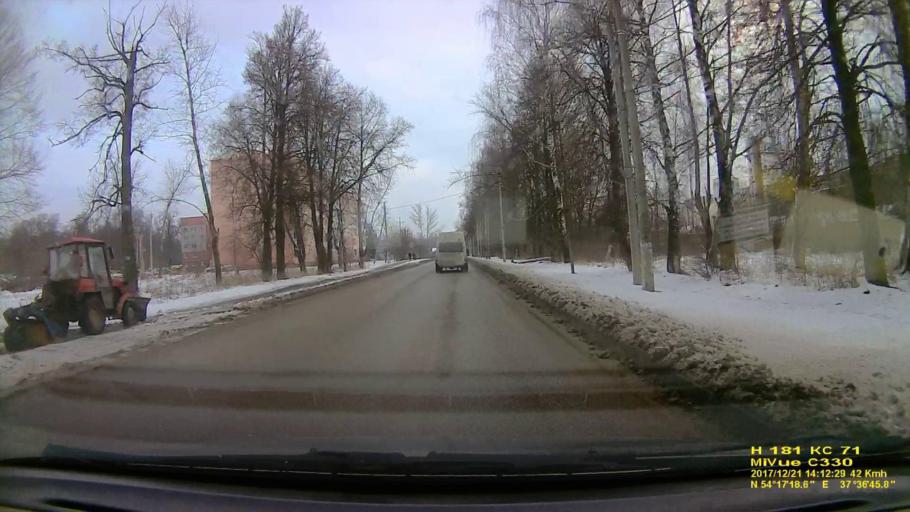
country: RU
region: Tula
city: Gorelki
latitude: 54.2885
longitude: 37.6128
